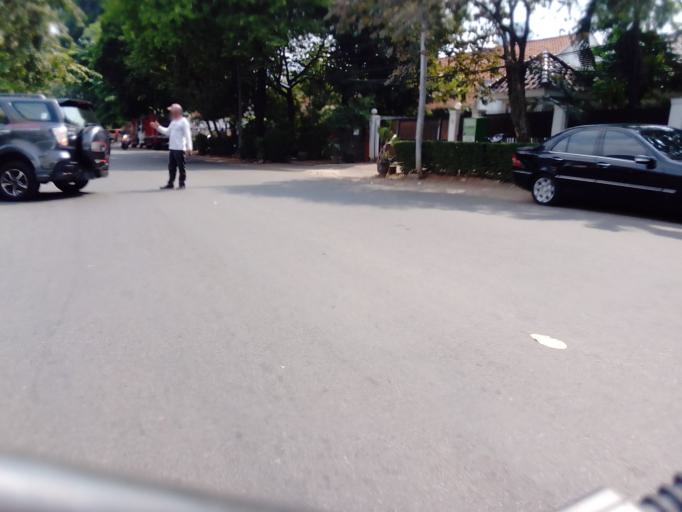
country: ID
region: Jakarta Raya
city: Jakarta
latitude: -6.2060
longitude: 106.8096
